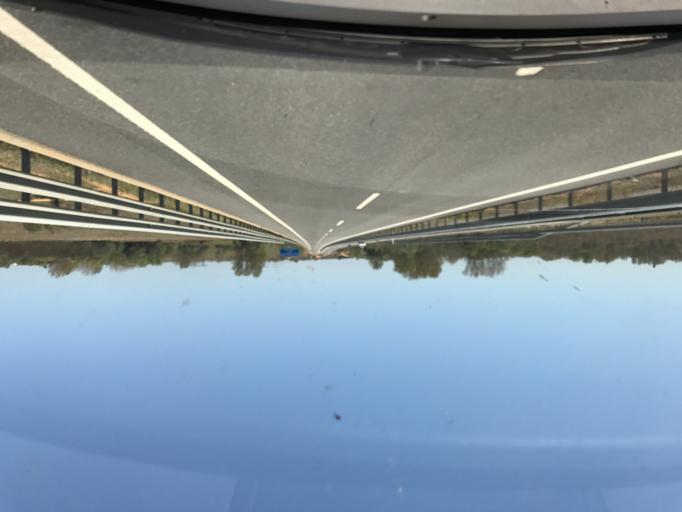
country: ES
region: Castille and Leon
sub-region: Provincia de Leon
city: Valverde de la Virgen
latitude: 42.5618
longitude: -5.6749
